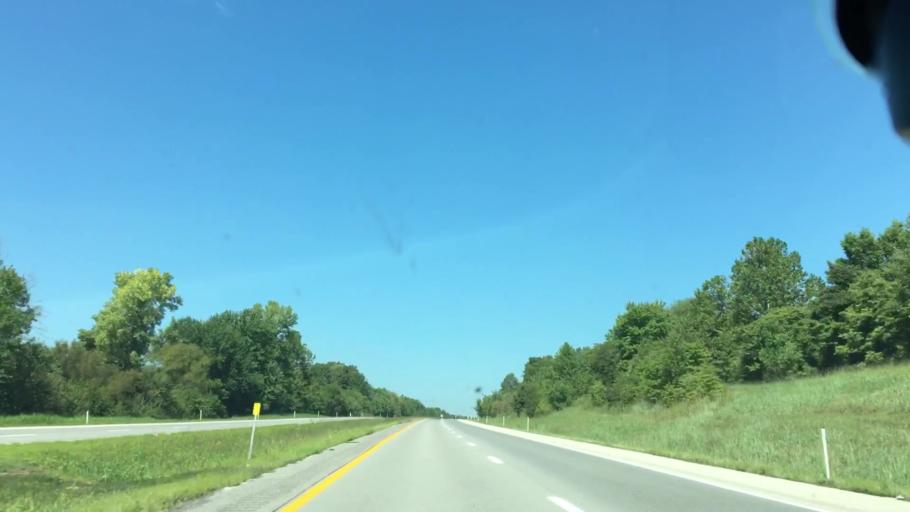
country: US
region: Kentucky
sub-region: Webster County
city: Sebree
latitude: 37.6524
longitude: -87.5124
